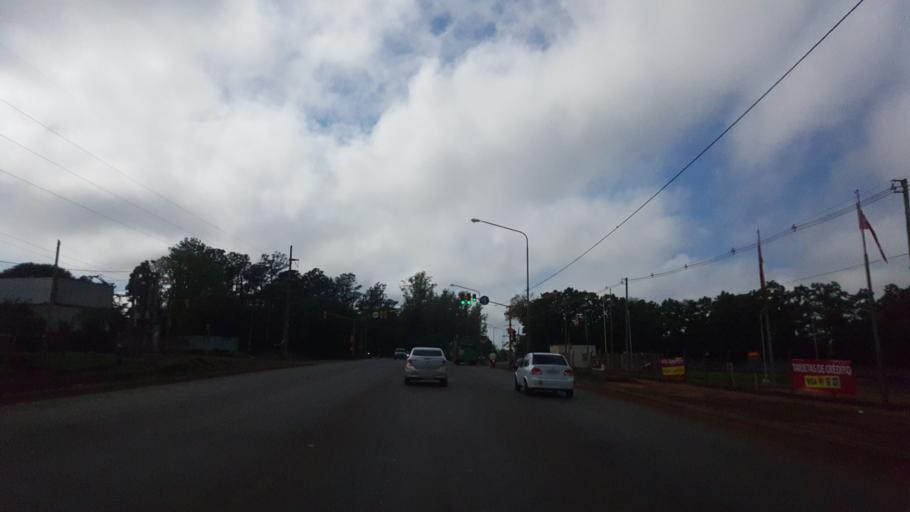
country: AR
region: Misiones
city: Garupa
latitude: -27.4406
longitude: -55.8784
